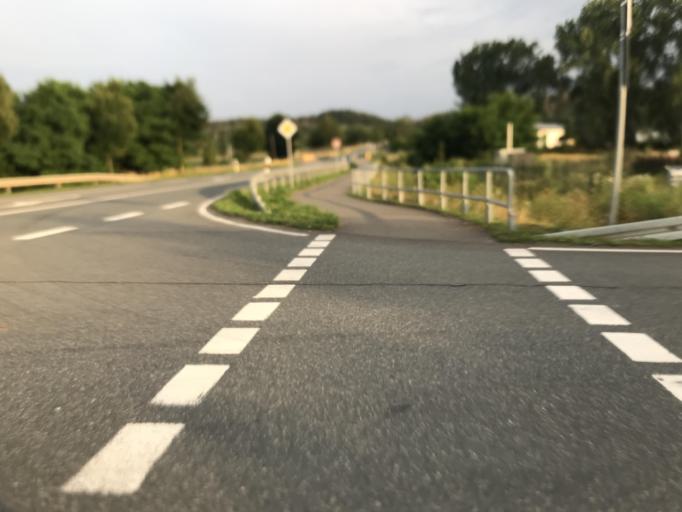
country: DE
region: Saxony-Anhalt
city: Quedlinburg
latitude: 51.8092
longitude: 11.1290
